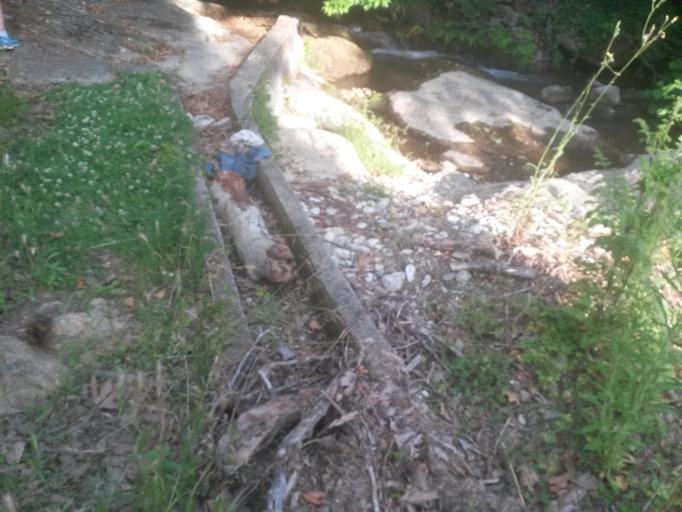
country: GR
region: North Aegean
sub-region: Nomos Lesvou
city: Agiasos
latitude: 39.0987
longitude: 26.3983
